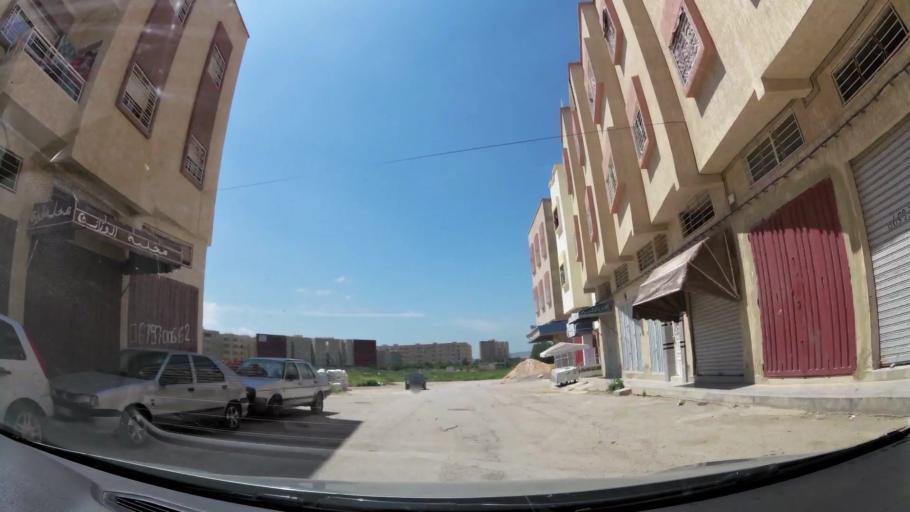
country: MA
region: Fes-Boulemane
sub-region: Fes
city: Fes
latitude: 34.0252
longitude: -5.0468
